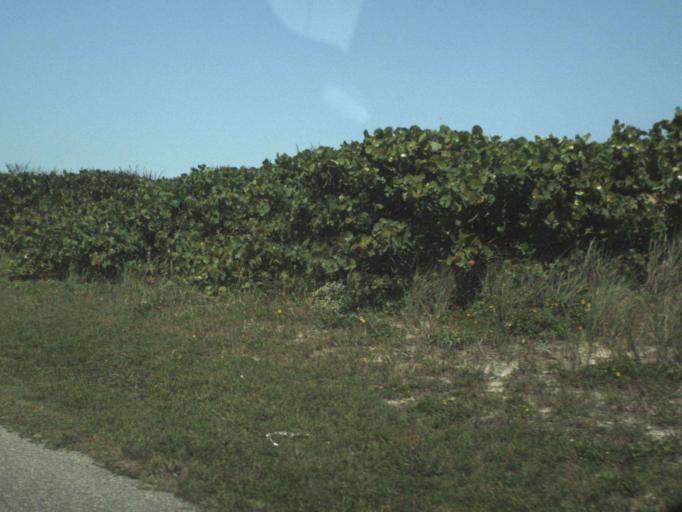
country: US
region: Florida
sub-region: Brevard County
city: South Patrick Shores
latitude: 28.2463
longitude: -80.6025
